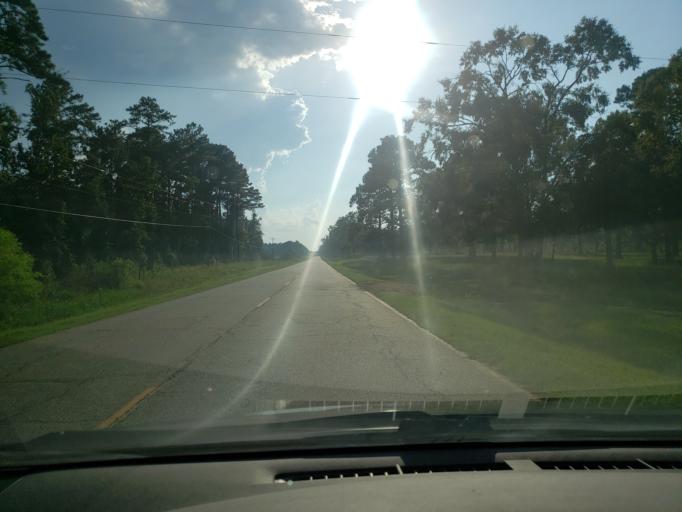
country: US
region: Georgia
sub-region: Dougherty County
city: Albany
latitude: 31.5737
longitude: -84.3163
